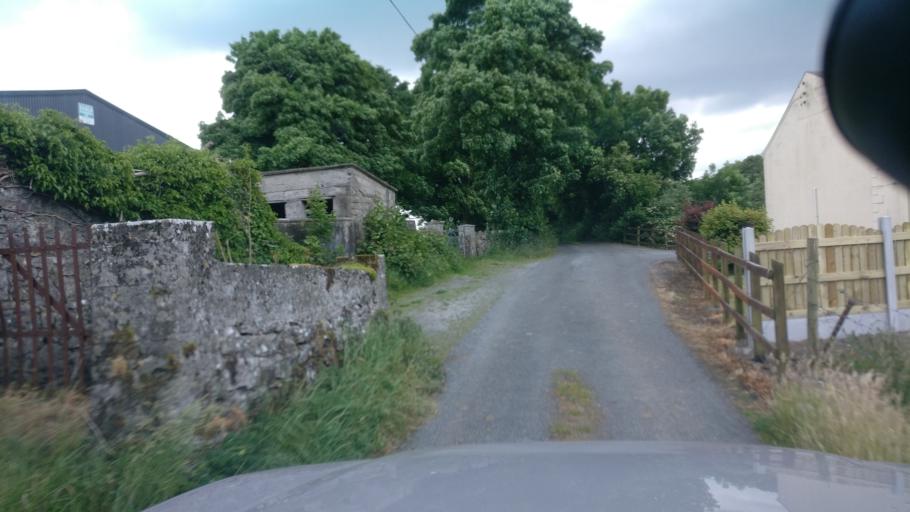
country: IE
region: Connaught
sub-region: County Galway
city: Ballinasloe
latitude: 53.3038
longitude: -8.2869
